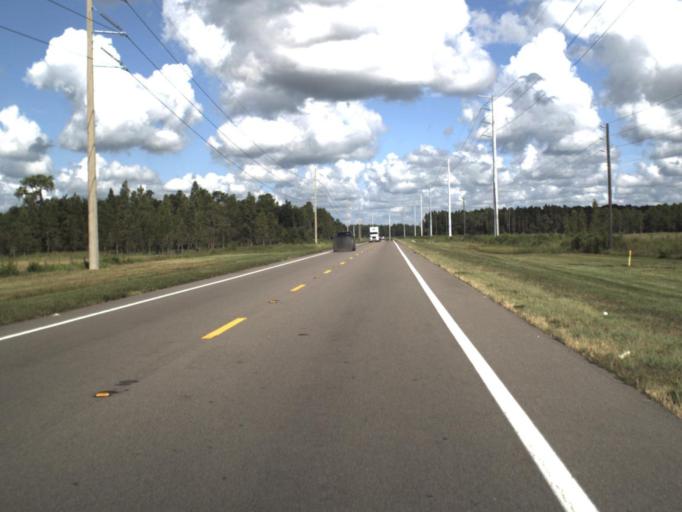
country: US
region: Florida
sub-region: Polk County
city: Kathleen
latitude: 28.2376
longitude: -82.0428
